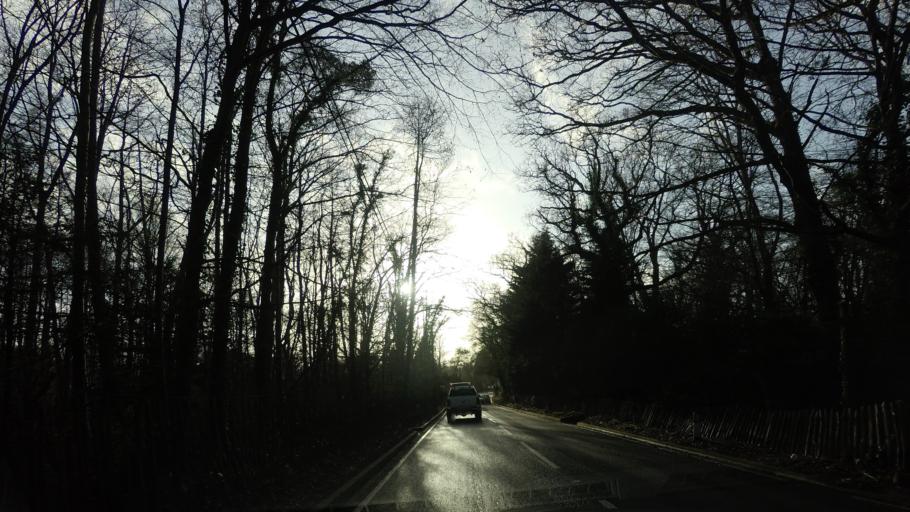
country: GB
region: England
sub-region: Kent
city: Tonbridge
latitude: 51.2219
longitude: 0.2883
